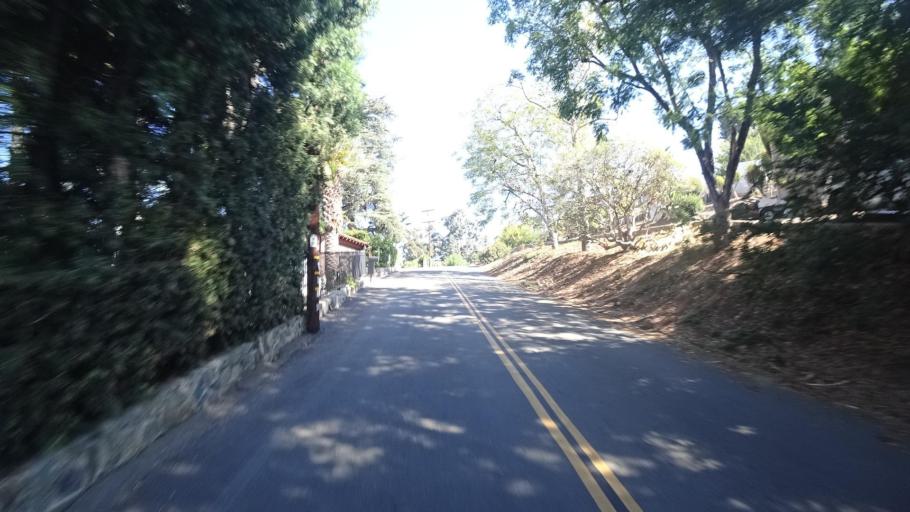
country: US
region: California
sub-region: San Diego County
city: Casa de Oro-Mount Helix
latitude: 32.7752
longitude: -116.9949
